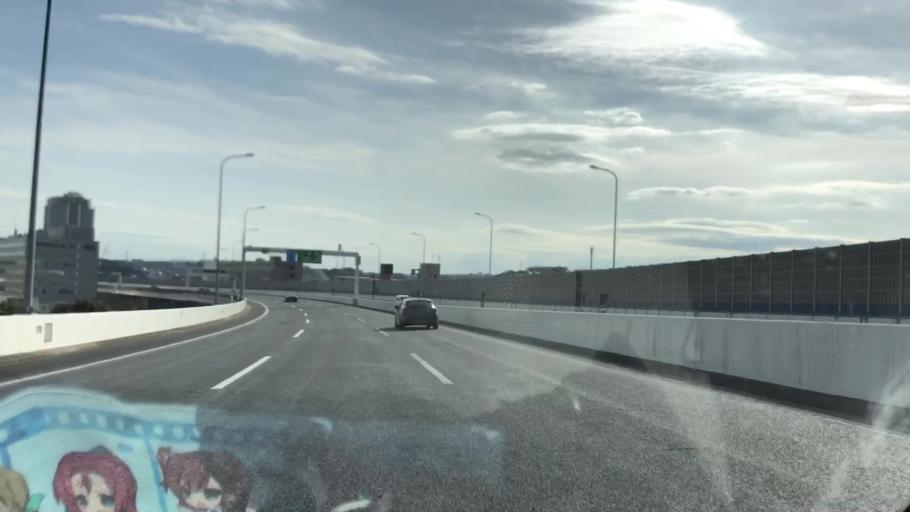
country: JP
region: Kanagawa
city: Yokohama
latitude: 35.3943
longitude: 139.6163
